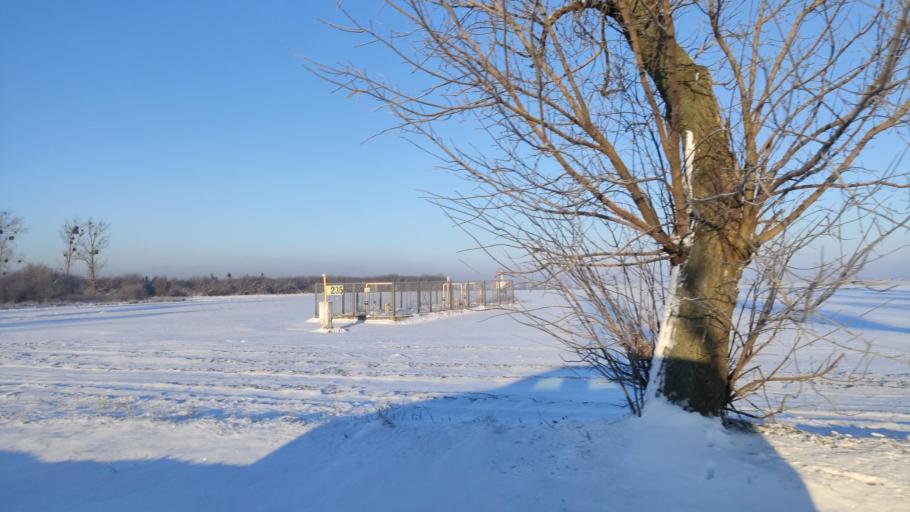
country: PL
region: Kujawsko-Pomorskie
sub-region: Powiat zninski
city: Znin
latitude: 52.8574
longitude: 17.7634
